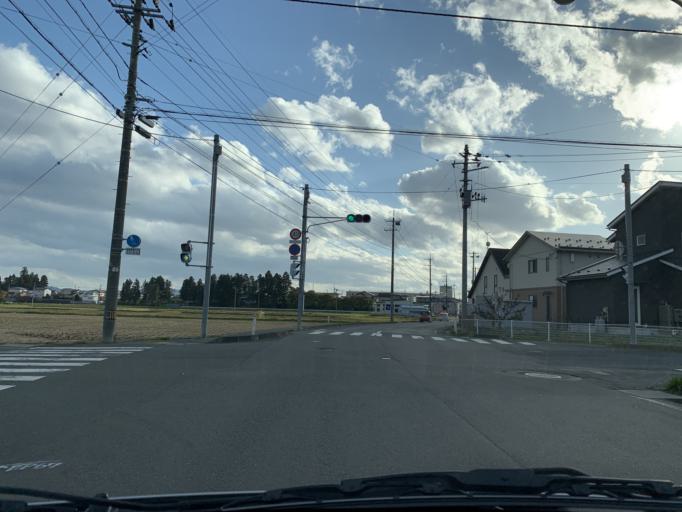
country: JP
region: Iwate
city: Mizusawa
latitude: 39.1436
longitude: 141.1589
